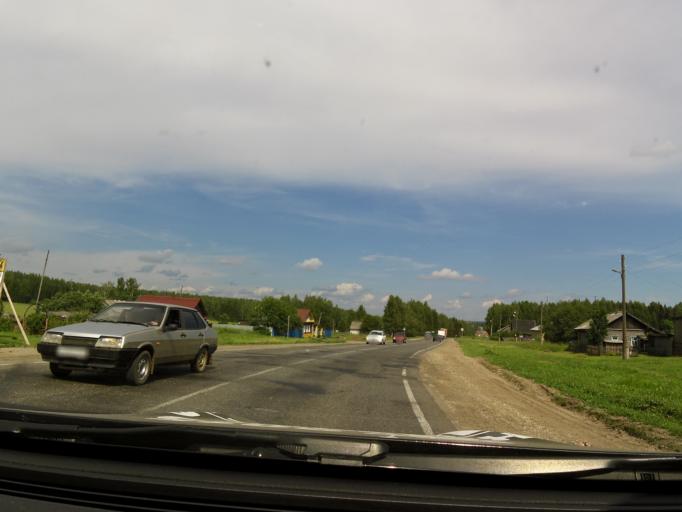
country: RU
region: Kirov
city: Vakhrushi
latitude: 58.6725
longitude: 49.9451
